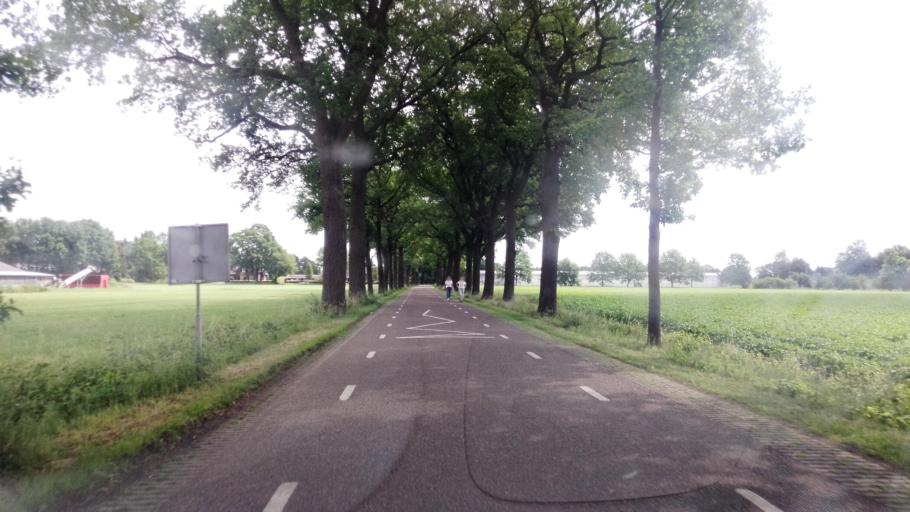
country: NL
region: Limburg
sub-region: Gemeente Venray
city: Venray
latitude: 51.4449
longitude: 6.0138
